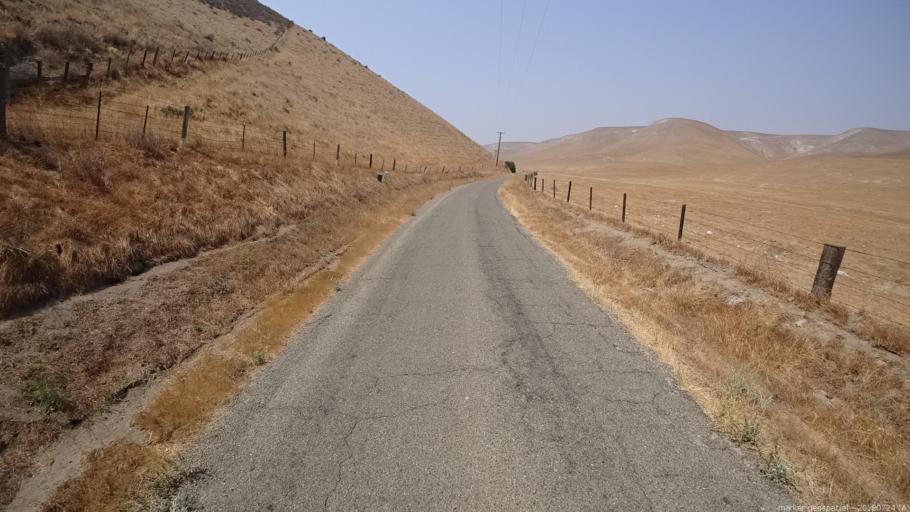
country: US
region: California
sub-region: Monterey County
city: King City
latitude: 36.1981
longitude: -121.0044
